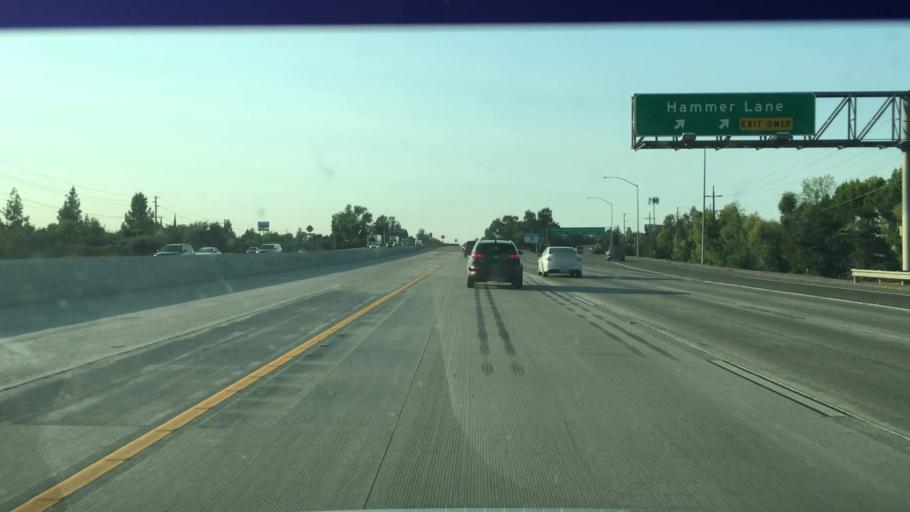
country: US
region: California
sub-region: San Joaquin County
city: Lincoln Village
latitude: 38.0179
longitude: -121.3570
